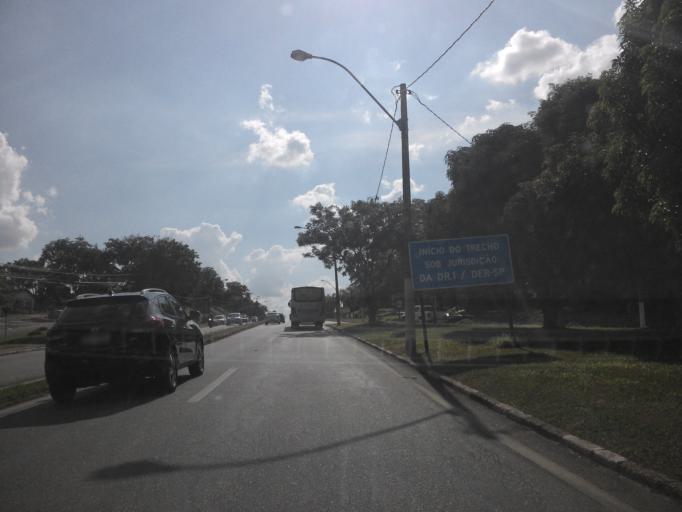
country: BR
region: Sao Paulo
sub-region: Valinhos
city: Valinhos
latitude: -22.9644
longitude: -47.0078
